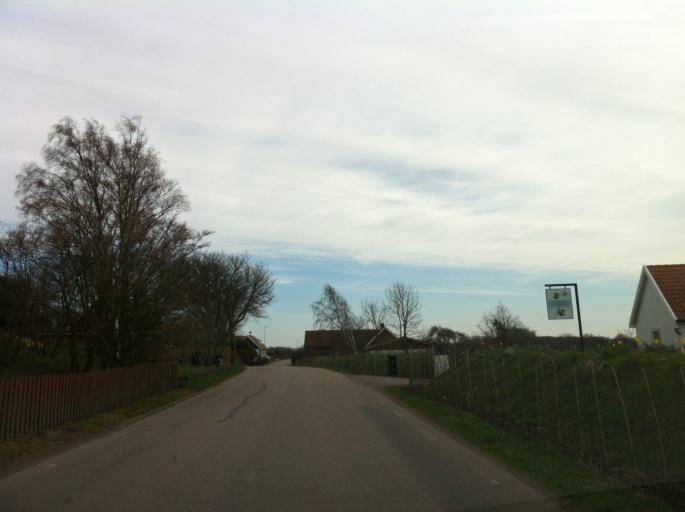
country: SE
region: Skane
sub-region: Hoganas Kommun
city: Hoganas
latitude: 56.2653
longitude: 12.5802
